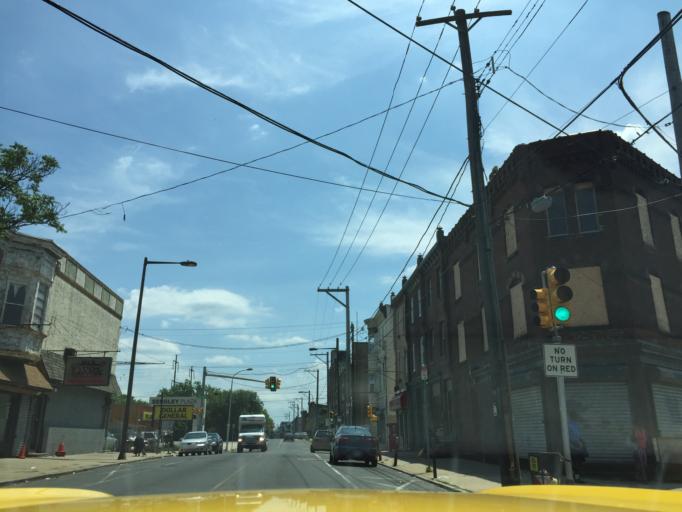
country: US
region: Pennsylvania
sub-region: Philadelphia County
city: Philadelphia
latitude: 39.9868
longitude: -75.1809
